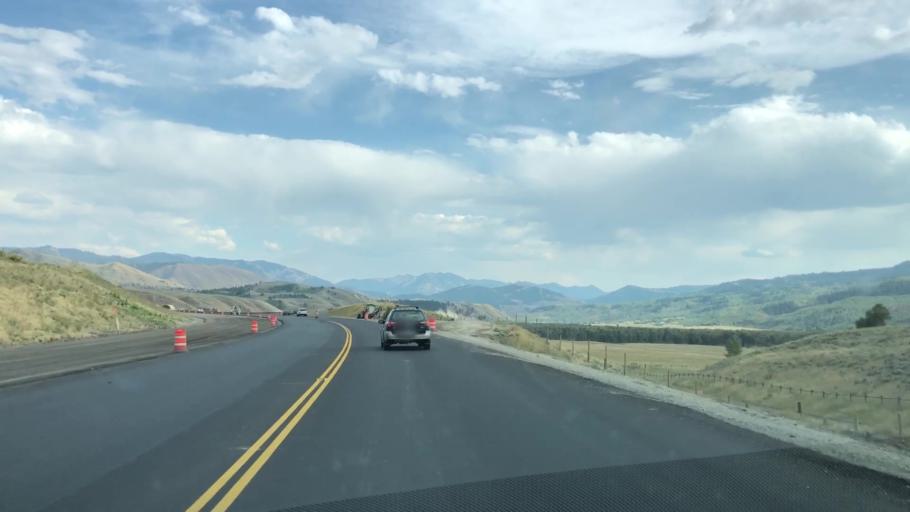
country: US
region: Wyoming
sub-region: Teton County
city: South Park
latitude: 43.4106
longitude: -110.7701
